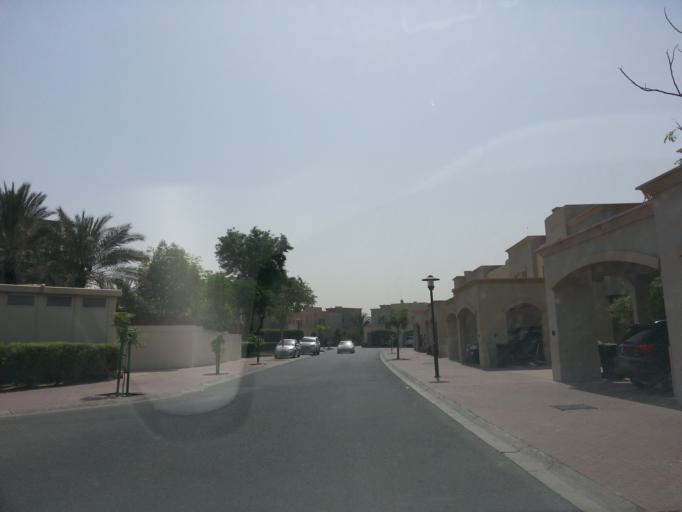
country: AE
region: Dubai
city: Dubai
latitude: 25.0534
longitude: 55.1728
